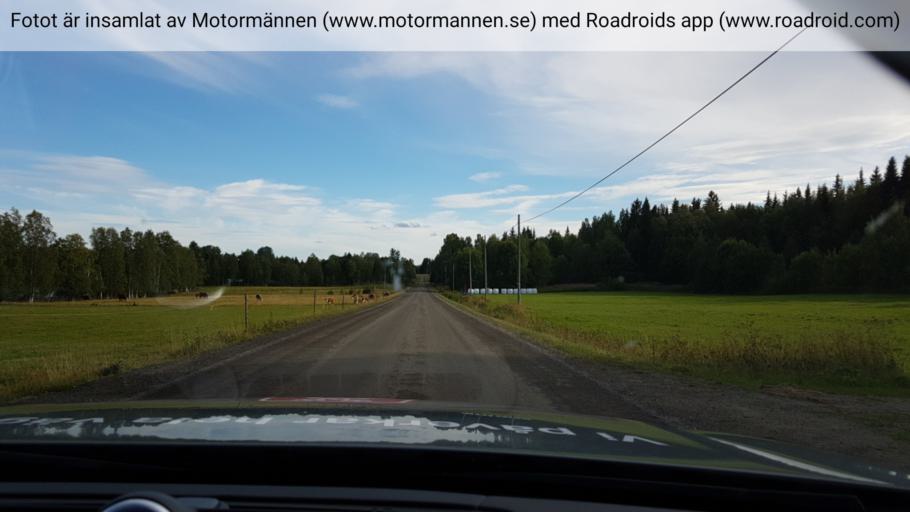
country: SE
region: Jaemtland
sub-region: Stroemsunds Kommun
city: Stroemsund
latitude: 64.0387
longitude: 15.8096
